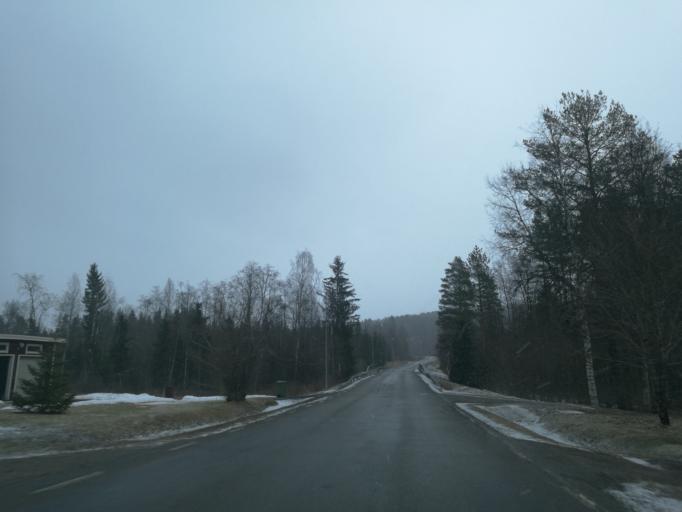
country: NO
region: Hedmark
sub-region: Grue
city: Kirkenaer
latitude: 60.7032
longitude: 12.6084
